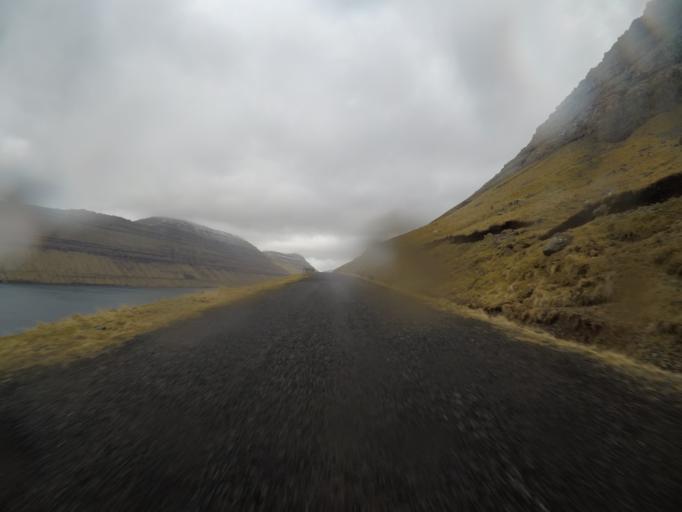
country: FO
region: Nordoyar
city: Klaksvik
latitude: 62.3310
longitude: -6.5728
